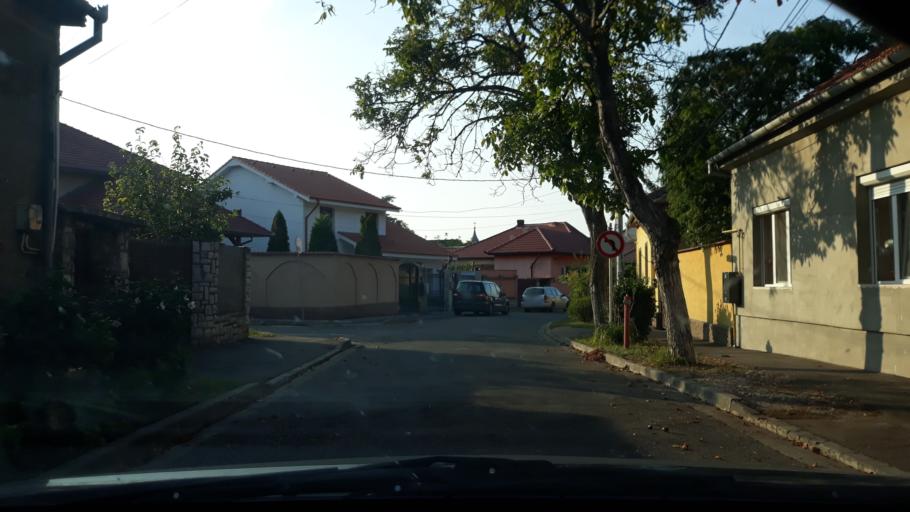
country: RO
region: Bihor
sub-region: Comuna Biharea
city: Oradea
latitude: 47.0473
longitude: 21.9471
